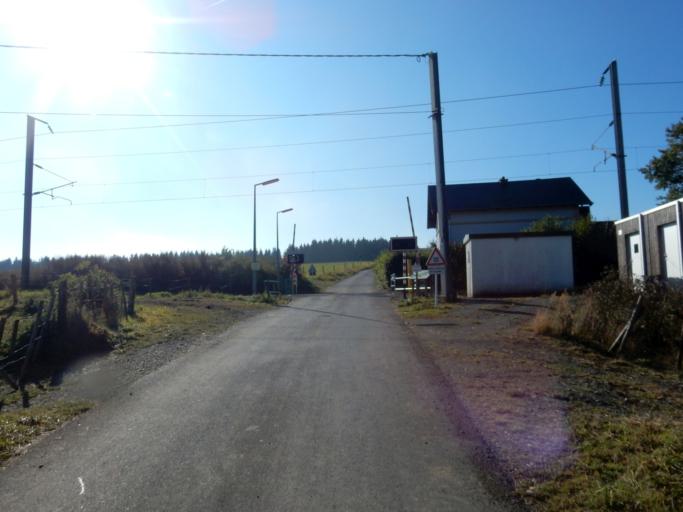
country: LU
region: Diekirch
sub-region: Canton de Clervaux
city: Troisvierges
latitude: 50.1338
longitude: 5.9843
